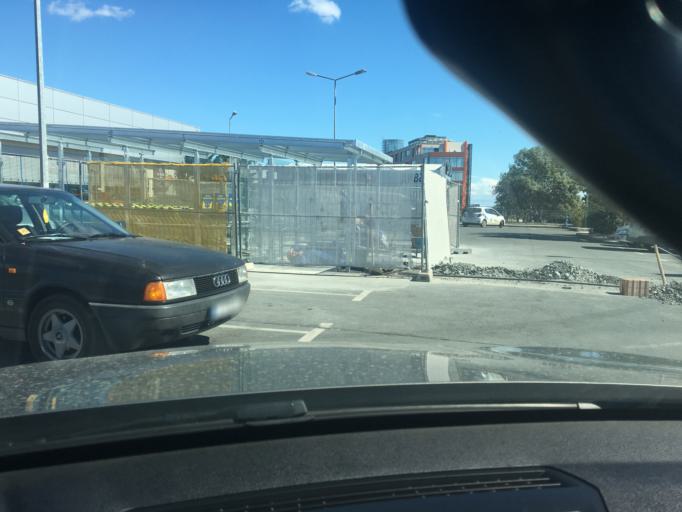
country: BG
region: Burgas
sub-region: Obshtina Burgas
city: Burgas
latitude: 42.5314
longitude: 27.4624
